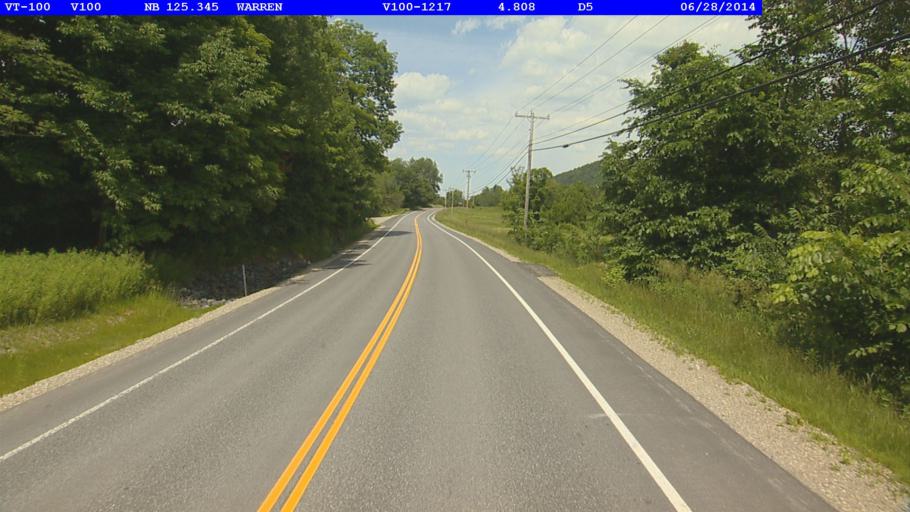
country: US
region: Vermont
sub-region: Washington County
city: Northfield
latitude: 44.1263
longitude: -72.8517
